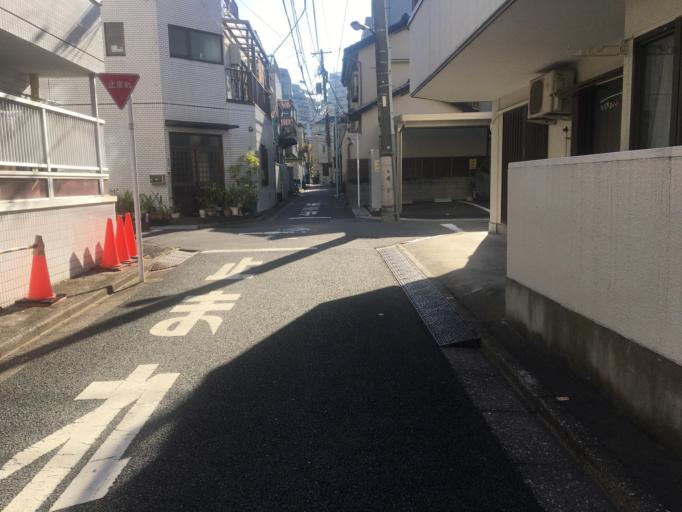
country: JP
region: Tokyo
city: Tokyo
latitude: 35.7362
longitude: 139.7072
